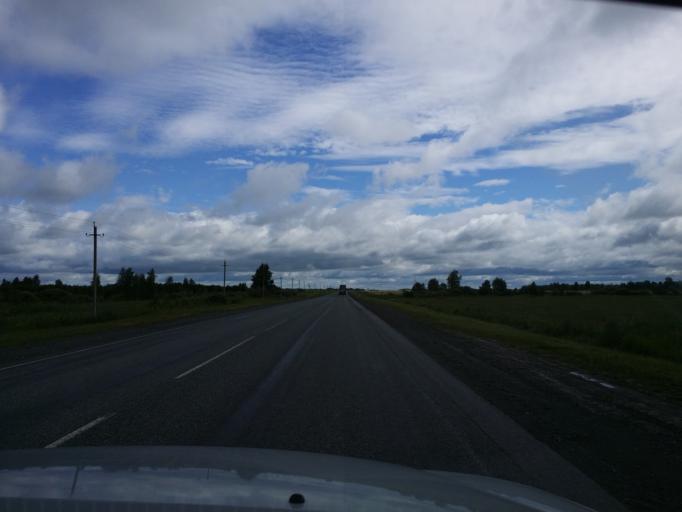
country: RU
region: Tjumen
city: Yarkovo
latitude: 57.2782
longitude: 66.8723
